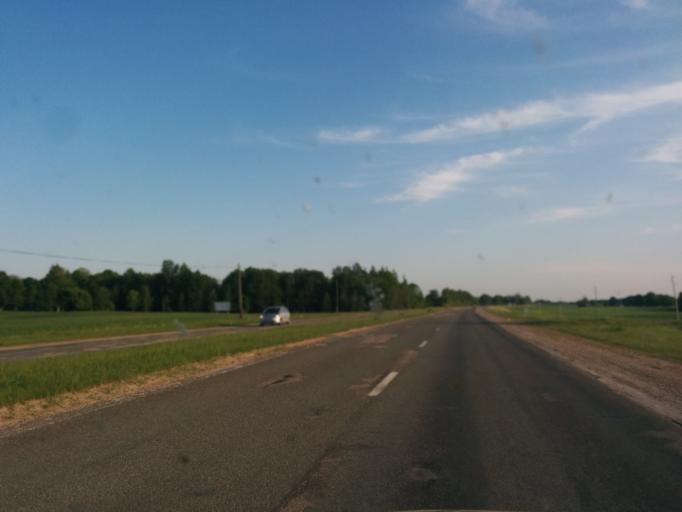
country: LV
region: Talsu Rajons
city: Talsi
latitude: 57.2288
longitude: 22.5846
